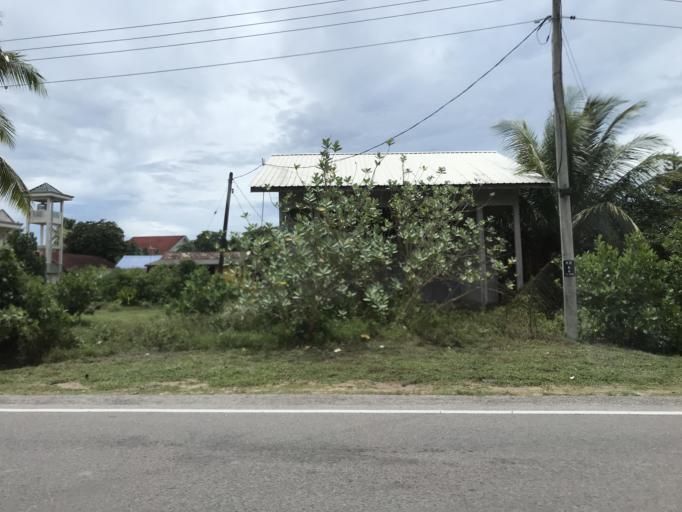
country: MY
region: Kelantan
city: Tumpat
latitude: 6.1758
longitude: 102.1968
